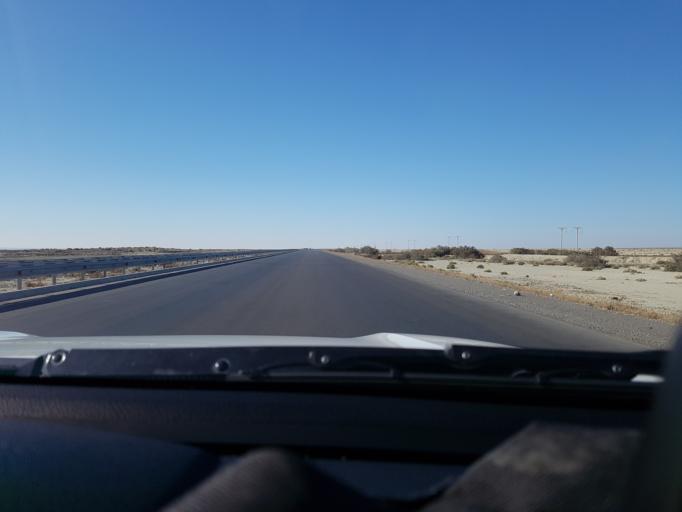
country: TM
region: Balkan
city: Gazanjyk
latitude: 39.2440
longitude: 55.0903
